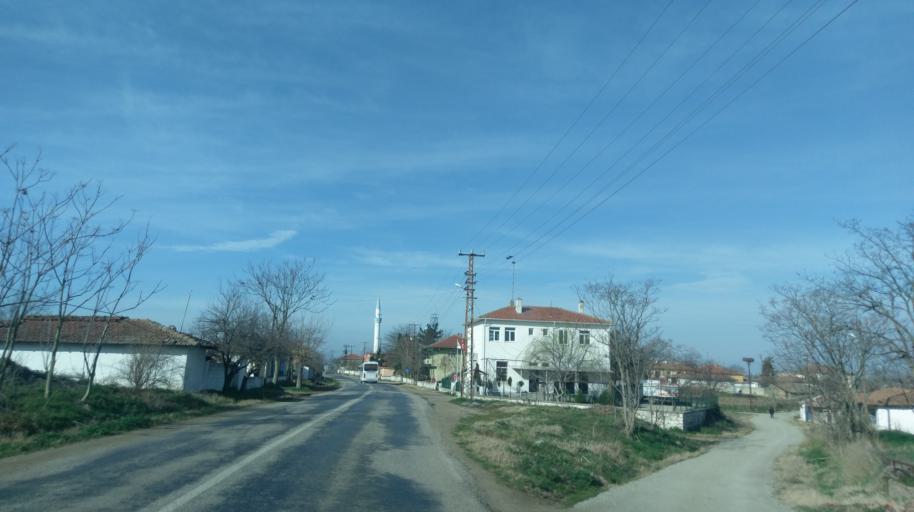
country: TR
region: Edirne
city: Copkoy
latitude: 41.3069
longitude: 26.8230
